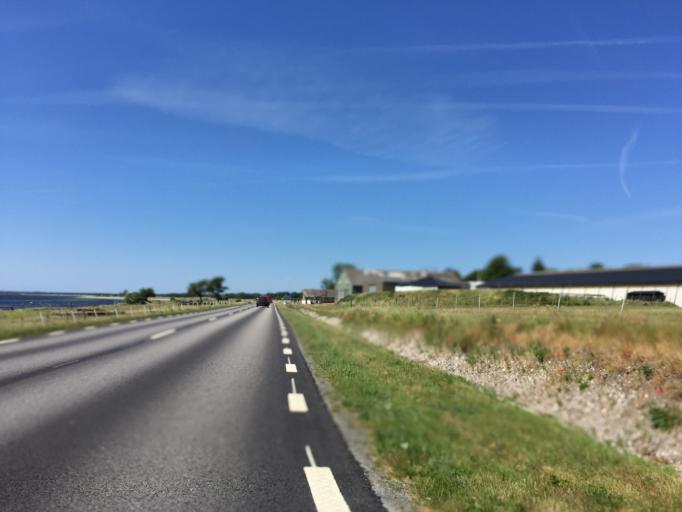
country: SE
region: Skane
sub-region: Trelleborgs Kommun
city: Skare
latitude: 55.3870
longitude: 13.0170
